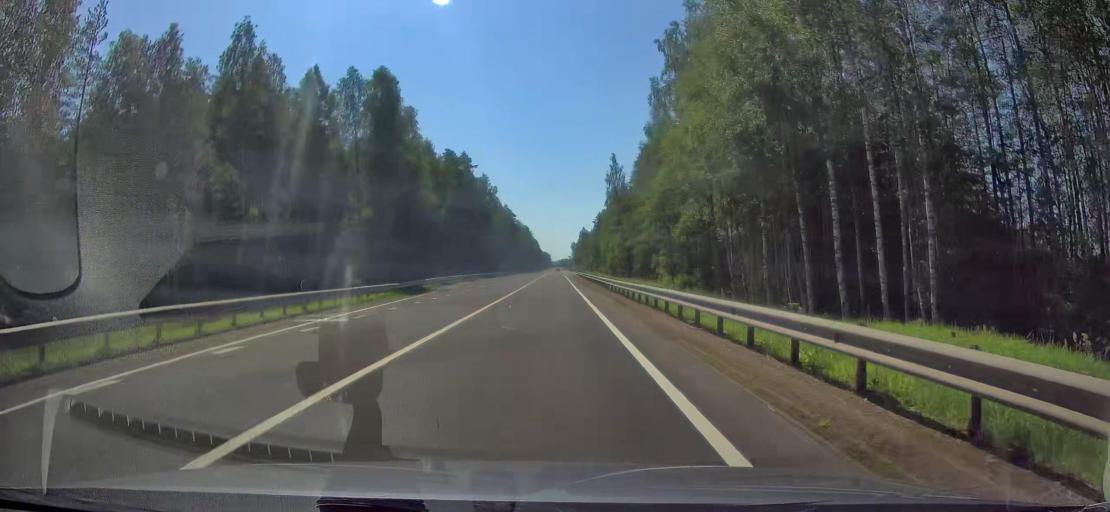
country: RU
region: Leningrad
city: Yefimovskiy
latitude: 59.3582
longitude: 34.8260
